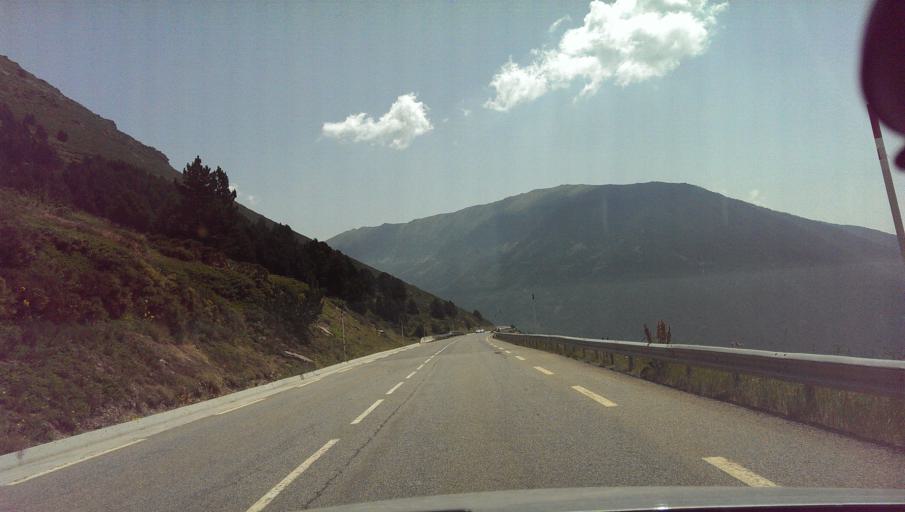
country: AD
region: Encamp
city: Pas de la Casa
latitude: 42.5576
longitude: 1.8169
